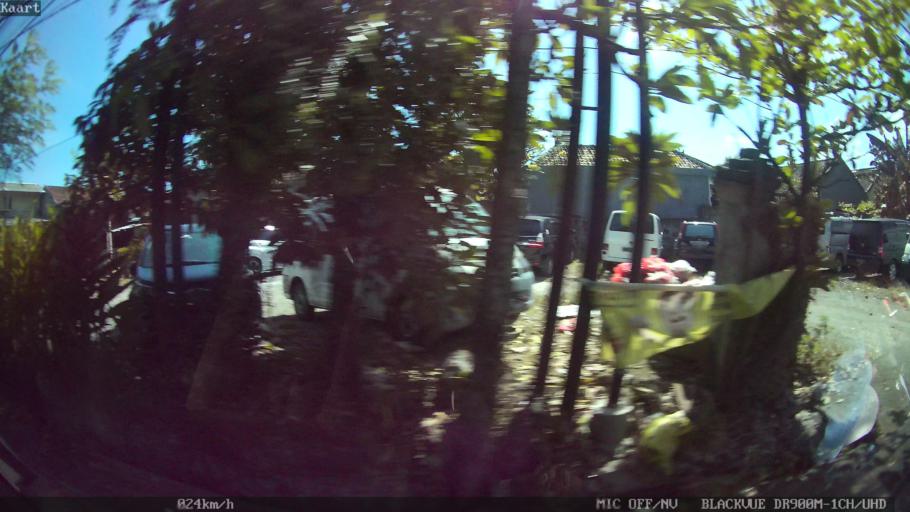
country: ID
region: Bali
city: Denpasar
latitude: -8.6729
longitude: 115.1826
